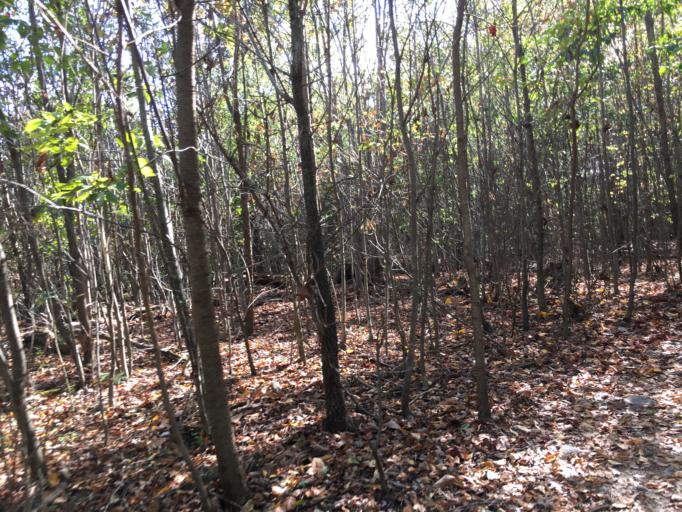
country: US
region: Pennsylvania
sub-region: York County
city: Yorklyn
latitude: 40.0093
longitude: -76.6481
